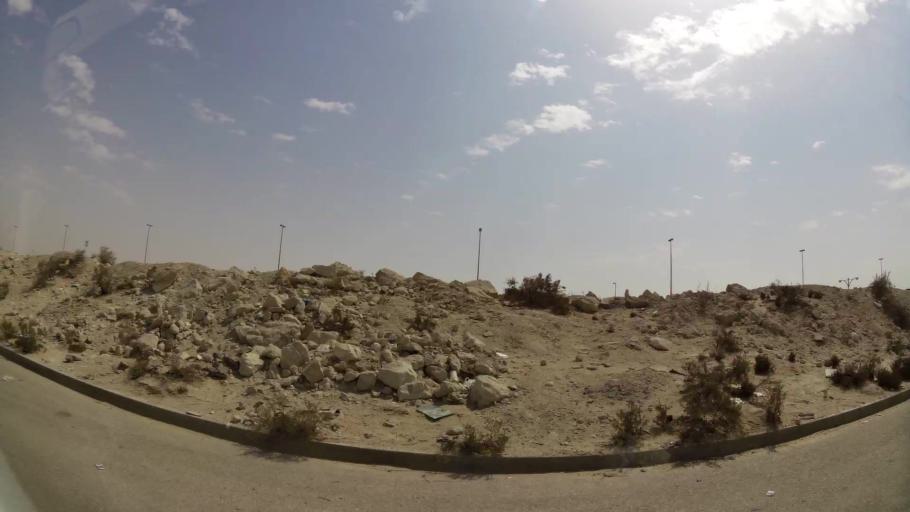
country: AE
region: Abu Dhabi
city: Abu Dhabi
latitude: 24.2996
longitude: 54.6319
